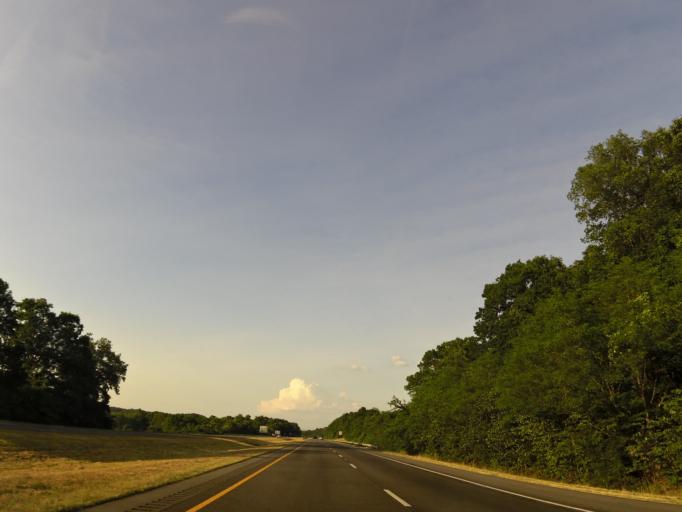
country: US
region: Alabama
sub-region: DeKalb County
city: Fort Payne
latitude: 34.4838
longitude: -85.7063
